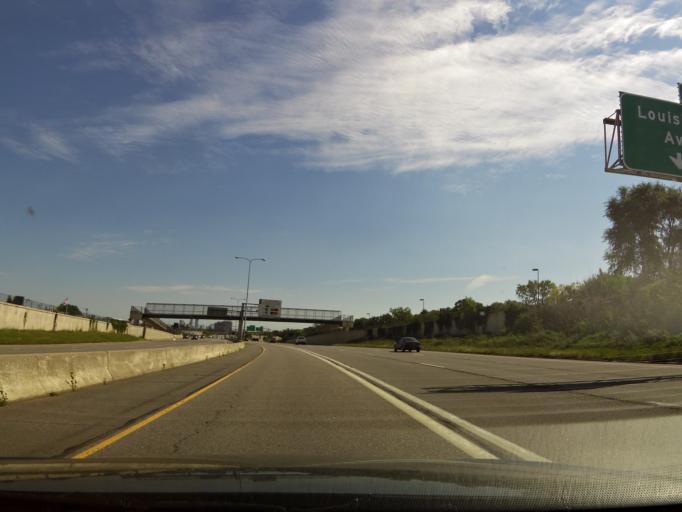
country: US
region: Minnesota
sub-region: Hennepin County
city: Saint Louis Park
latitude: 44.9713
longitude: -93.3794
